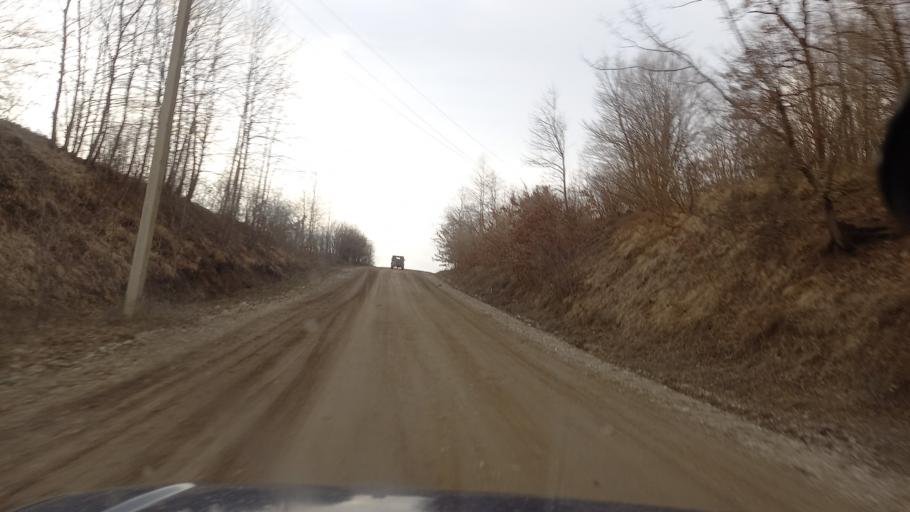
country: RU
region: Adygeya
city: Kamennomostskiy
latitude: 44.1936
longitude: 40.2577
